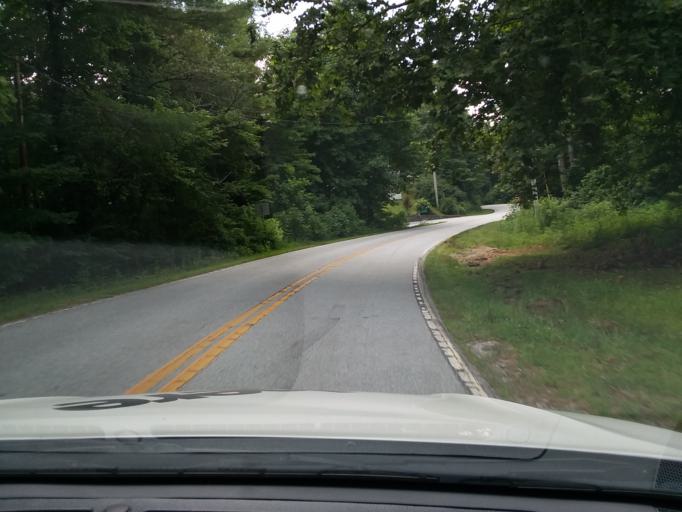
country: US
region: Georgia
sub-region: Rabun County
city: Mountain City
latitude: 35.0043
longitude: -83.2018
